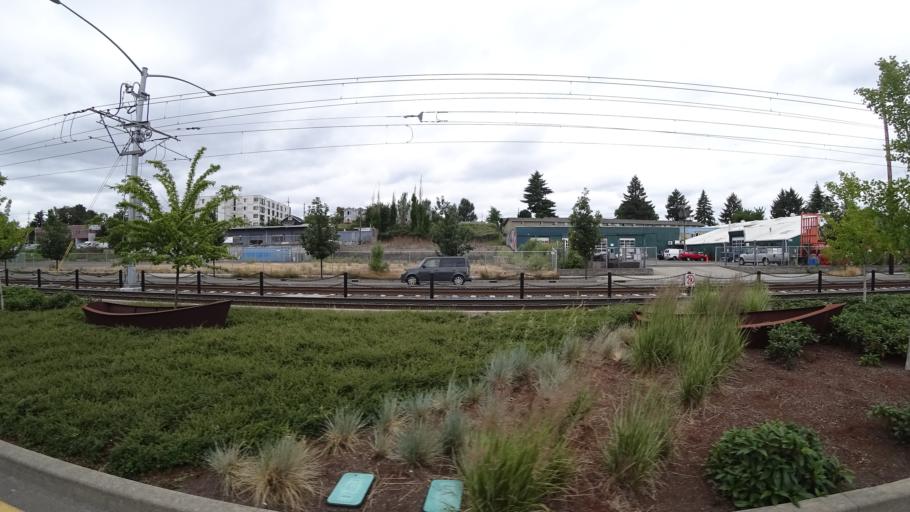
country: US
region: Oregon
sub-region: Clackamas County
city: Milwaukie
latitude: 45.4886
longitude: -122.6484
